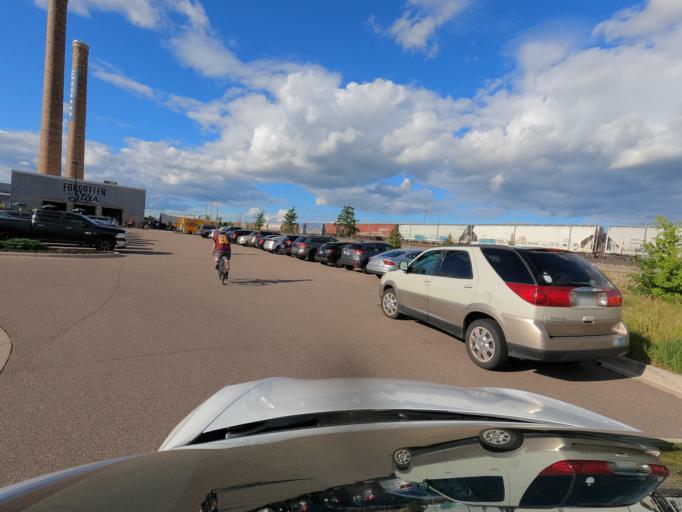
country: US
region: Minnesota
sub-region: Anoka County
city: Columbia Heights
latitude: 45.0550
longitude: -93.2733
